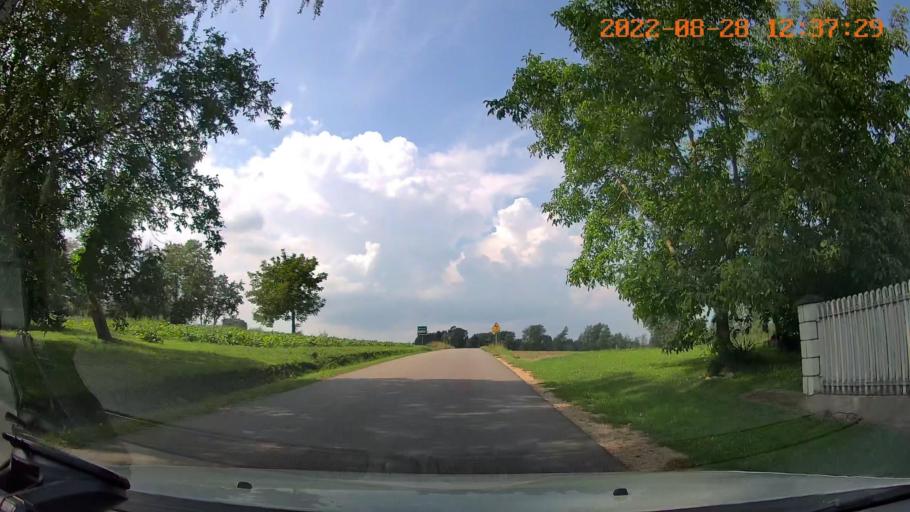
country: PL
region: Swietokrzyskie
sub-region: Powiat pinczowski
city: Dzialoszyce
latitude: 50.3682
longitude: 20.3980
